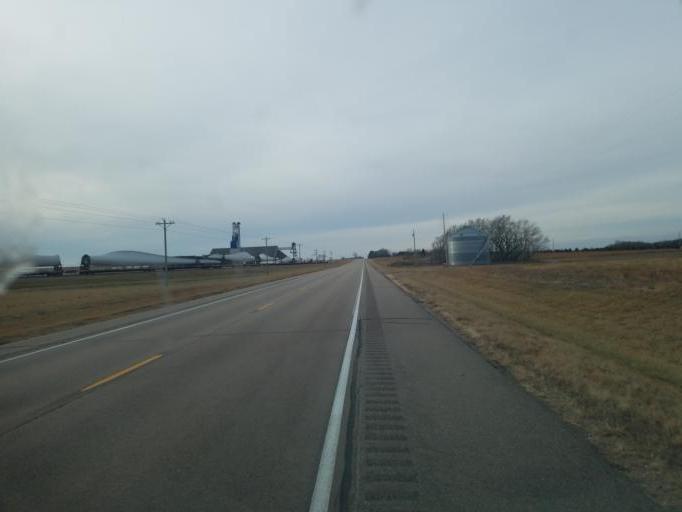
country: US
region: Nebraska
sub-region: Antelope County
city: Neligh
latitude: 42.3351
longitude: -98.1721
